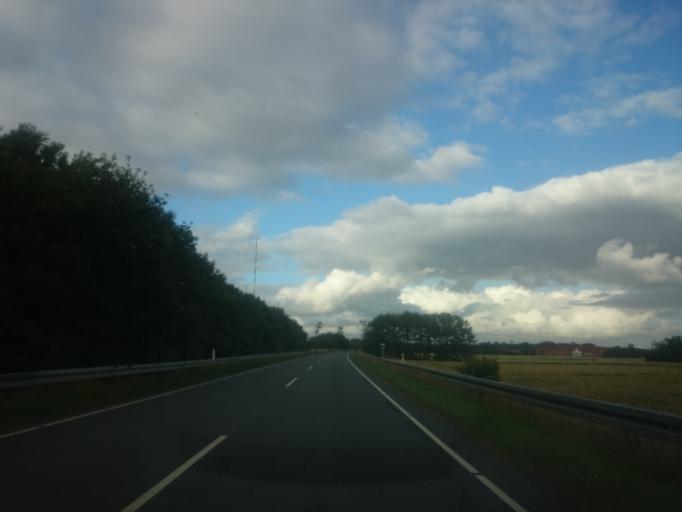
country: DK
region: South Denmark
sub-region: Varde Kommune
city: Olgod
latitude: 55.6489
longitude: 8.6520
